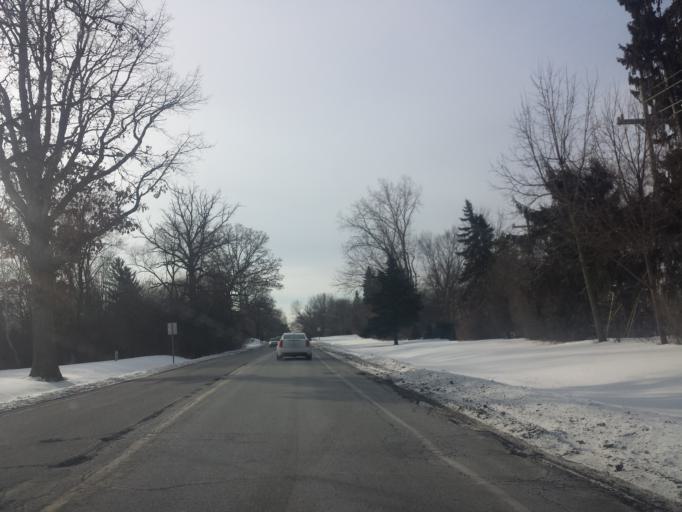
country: US
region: Michigan
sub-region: Oakland County
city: Franklin
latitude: 42.5414
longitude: -83.3410
